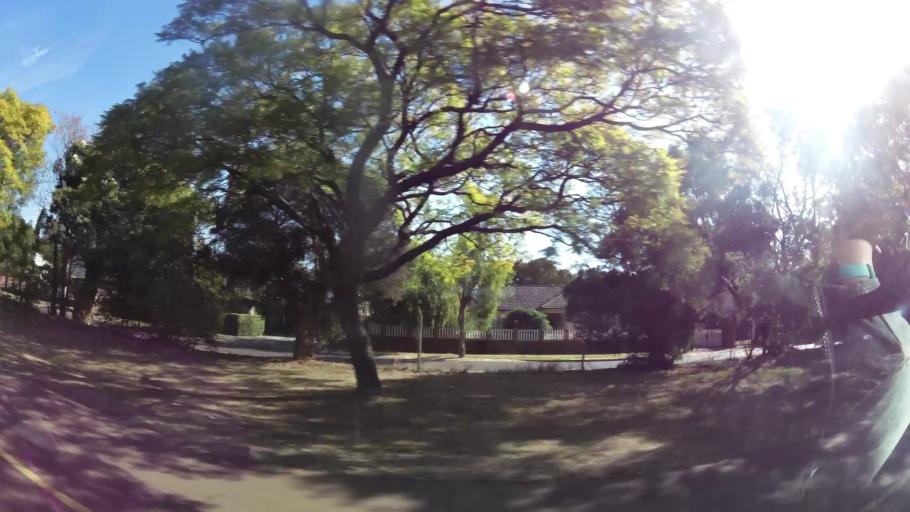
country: ZA
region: Gauteng
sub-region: City of Tshwane Metropolitan Municipality
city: Pretoria
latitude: -25.7296
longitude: 28.2585
